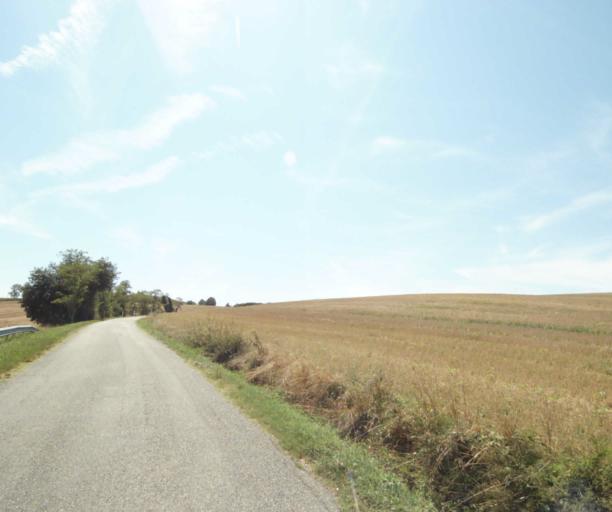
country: FR
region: Midi-Pyrenees
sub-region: Departement de l'Ariege
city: Lezat-sur-Leze
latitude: 43.2591
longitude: 1.3194
